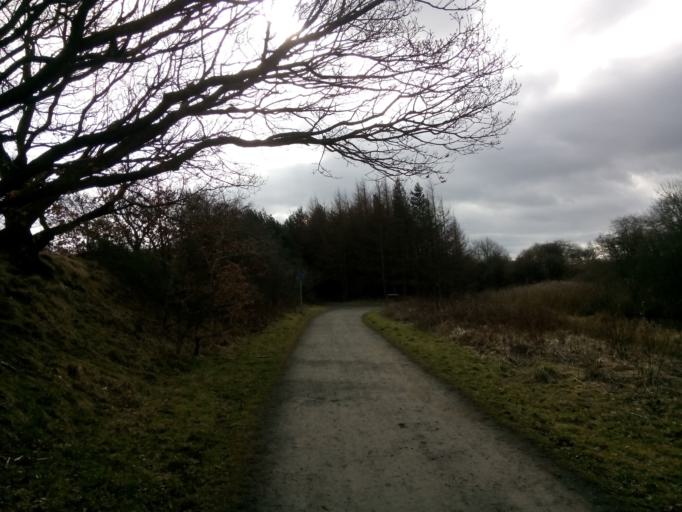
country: GB
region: England
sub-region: County Durham
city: Durham
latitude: 54.7740
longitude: -1.6067
